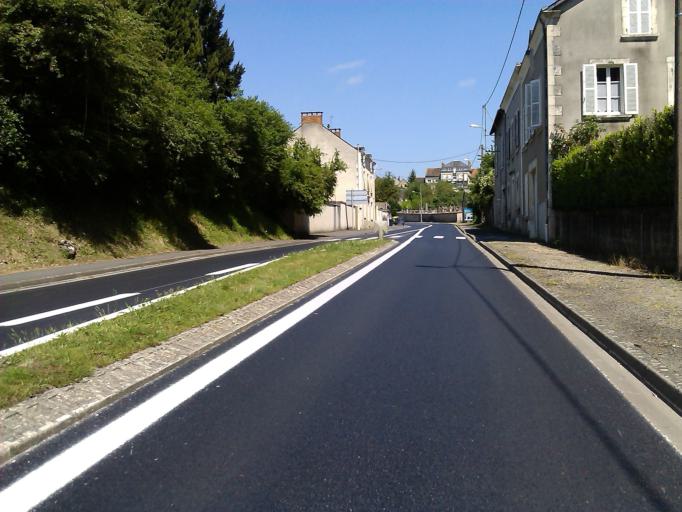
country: FR
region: Centre
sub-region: Departement de l'Indre
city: Saint-Marcel
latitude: 46.5989
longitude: 1.5120
